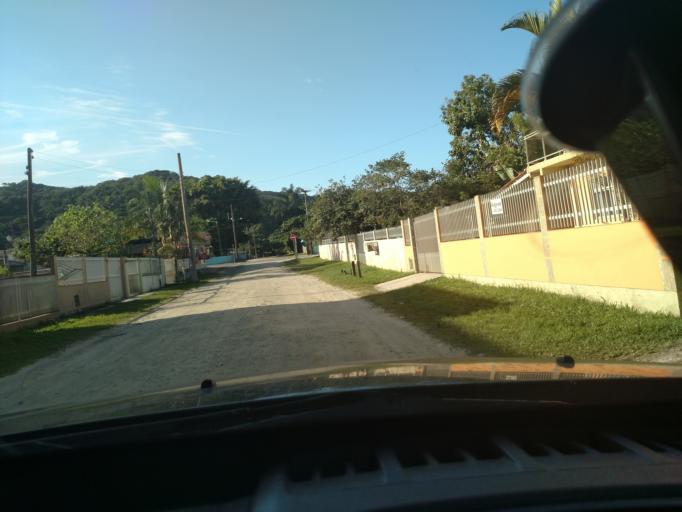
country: BR
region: Santa Catarina
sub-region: Porto Belo
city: Porto Belo
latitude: -27.1793
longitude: -48.5319
